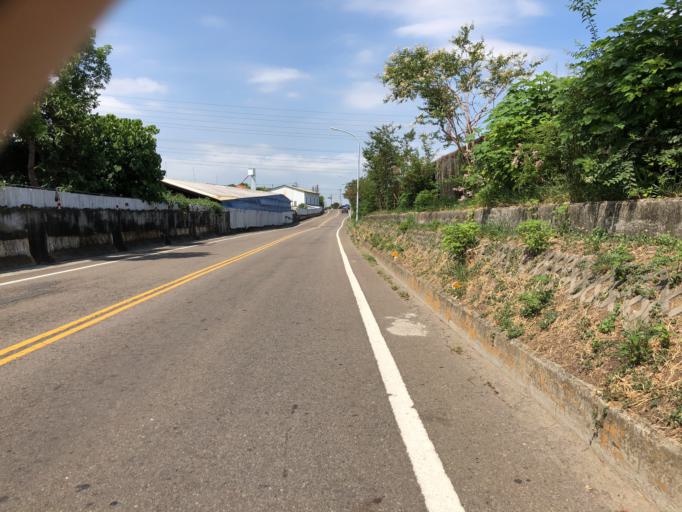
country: TW
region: Taiwan
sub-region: Taichung City
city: Taichung
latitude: 24.0748
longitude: 120.6949
